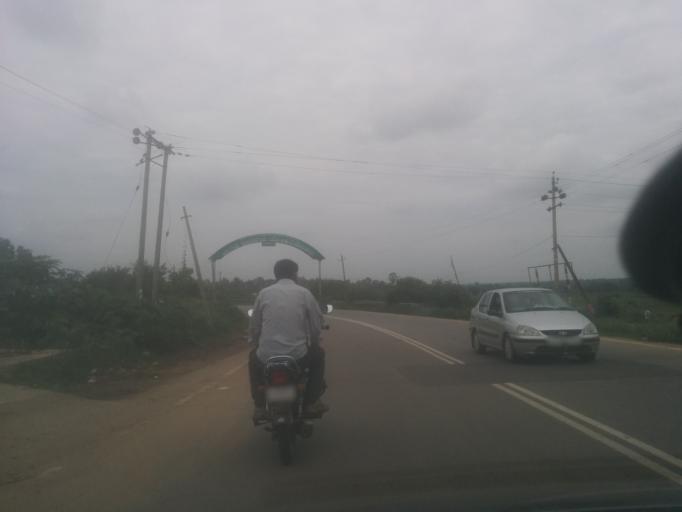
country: IN
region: Karnataka
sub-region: Hassan
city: Belur
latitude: 13.1692
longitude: 75.8772
